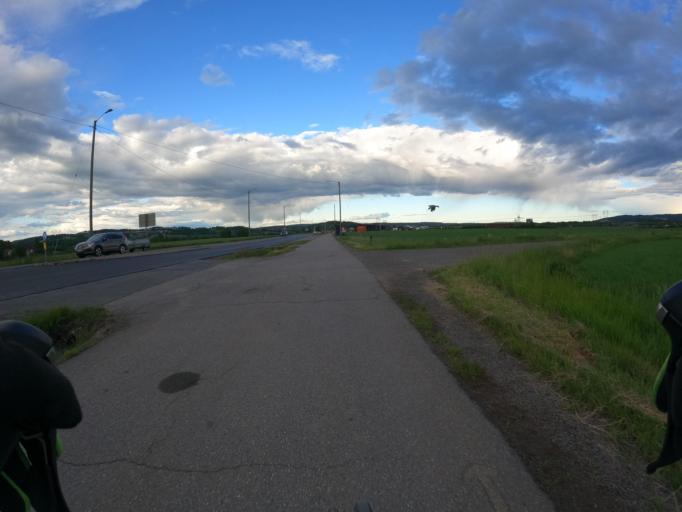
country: NO
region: Akershus
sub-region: Lorenskog
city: Kjenn
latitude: 59.9813
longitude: 10.9790
